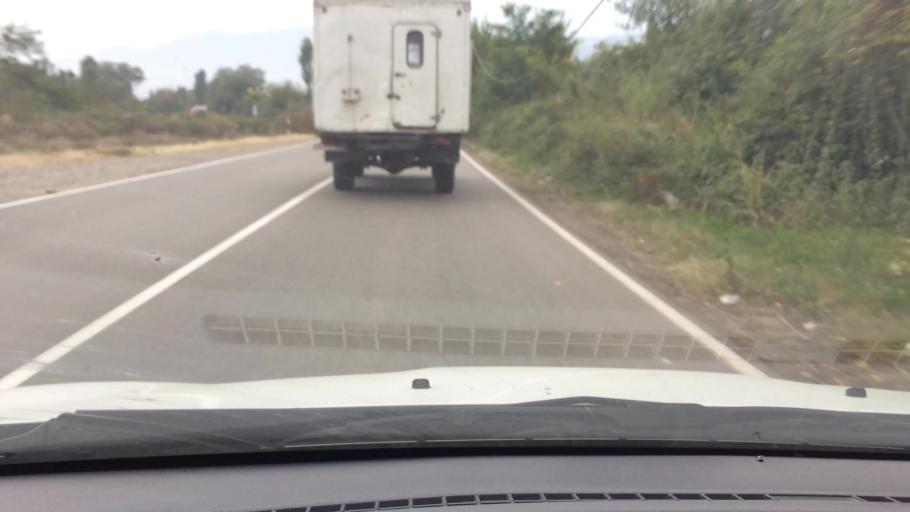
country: AM
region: Tavush
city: Bagratashen
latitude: 41.2642
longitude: 44.7942
